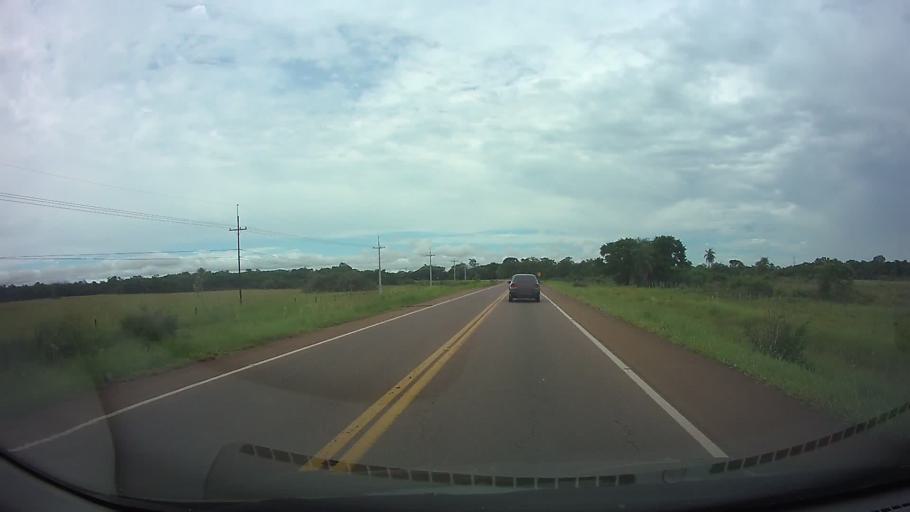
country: PY
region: Paraguari
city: Carapegua
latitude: -25.7214
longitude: -57.2020
